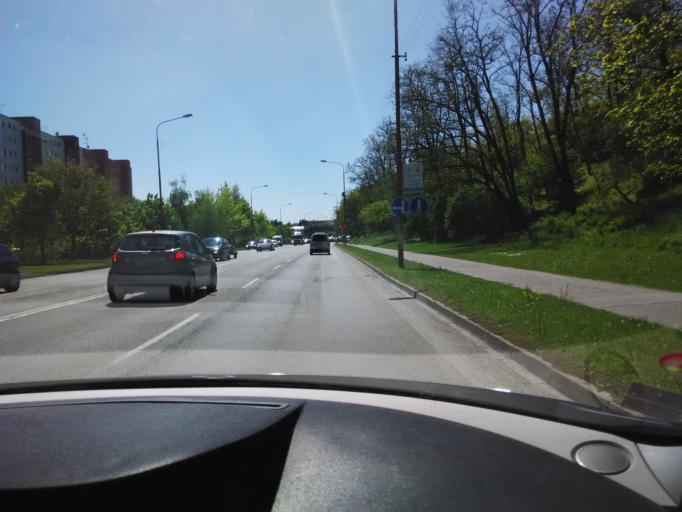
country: SK
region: Trnavsky
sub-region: Okres Trnava
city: Trnava
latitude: 48.3774
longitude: 17.5935
